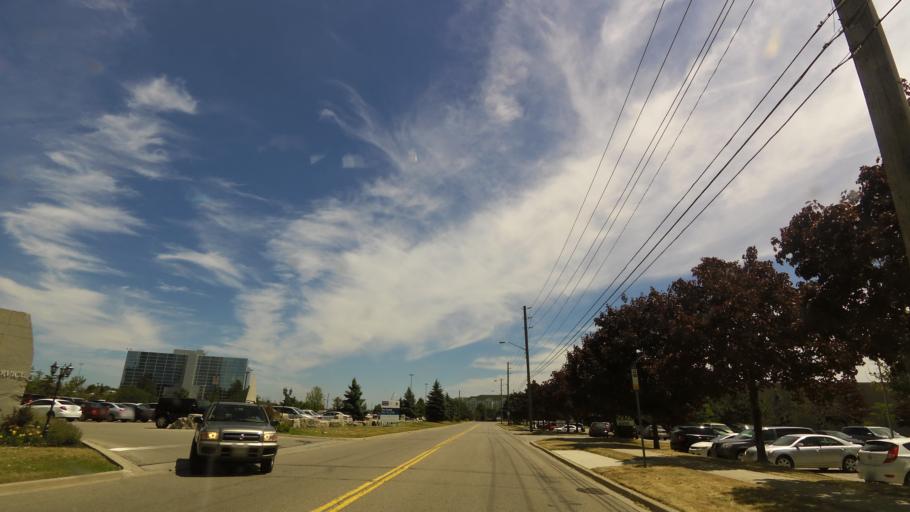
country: CA
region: Ontario
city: Burlington
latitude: 43.3957
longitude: -79.7617
